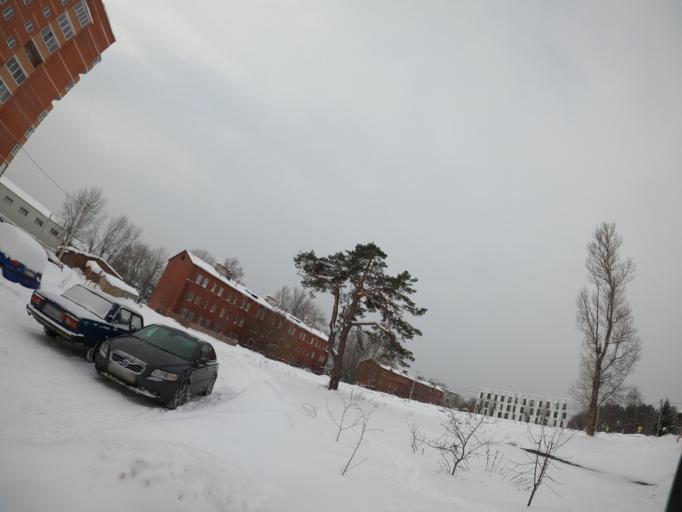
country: RU
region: Moskovskaya
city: Elektrogorsk
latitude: 55.8889
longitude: 38.7741
